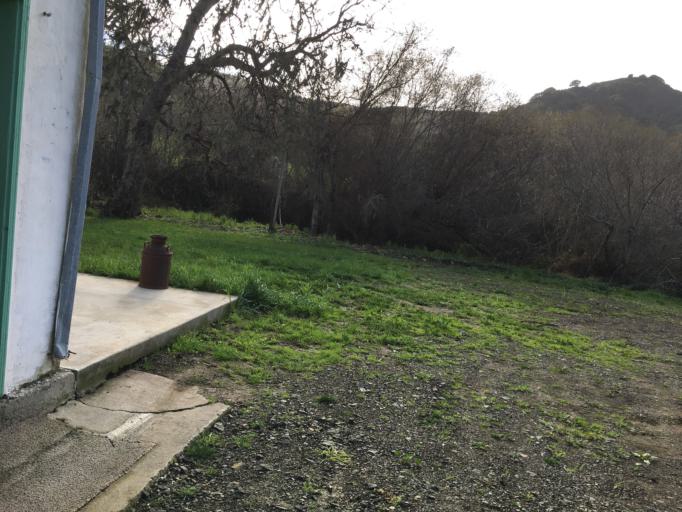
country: US
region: California
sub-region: San Luis Obispo County
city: Los Osos
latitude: 35.2837
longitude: -120.7947
